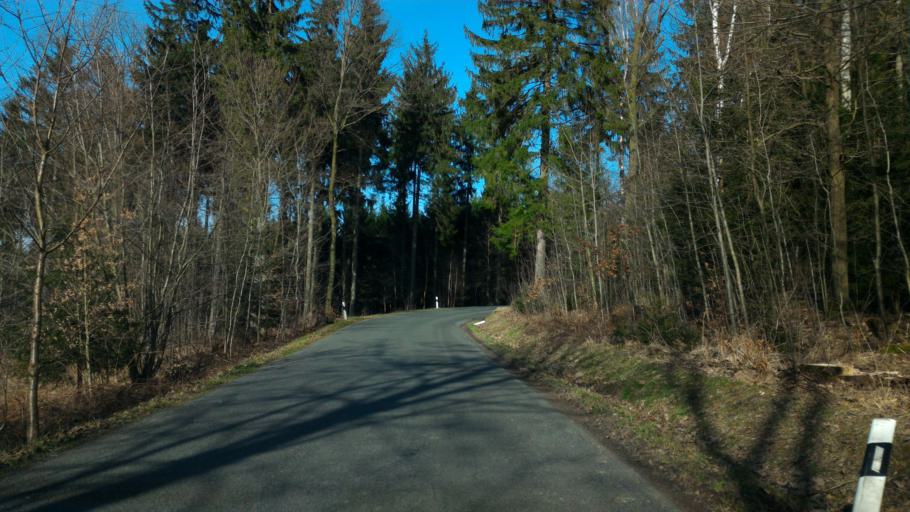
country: DE
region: Saxony
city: Durrrohrsdorf
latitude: 51.0271
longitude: 13.9689
